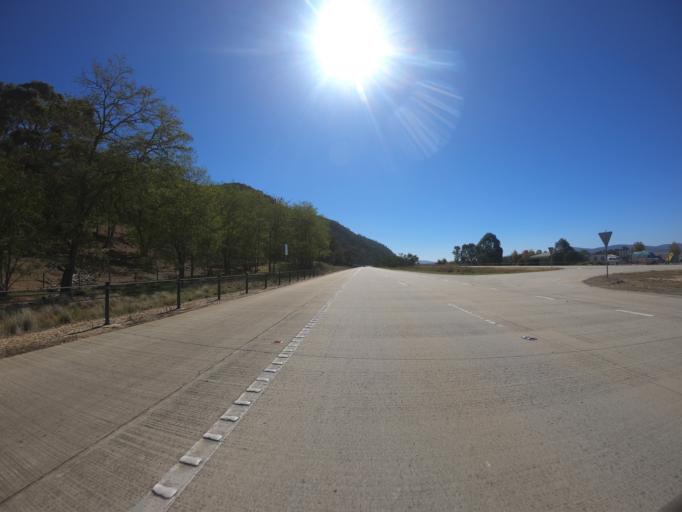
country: AU
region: New South Wales
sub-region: Yass Valley
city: Gundaroo
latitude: -35.0678
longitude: 149.3734
